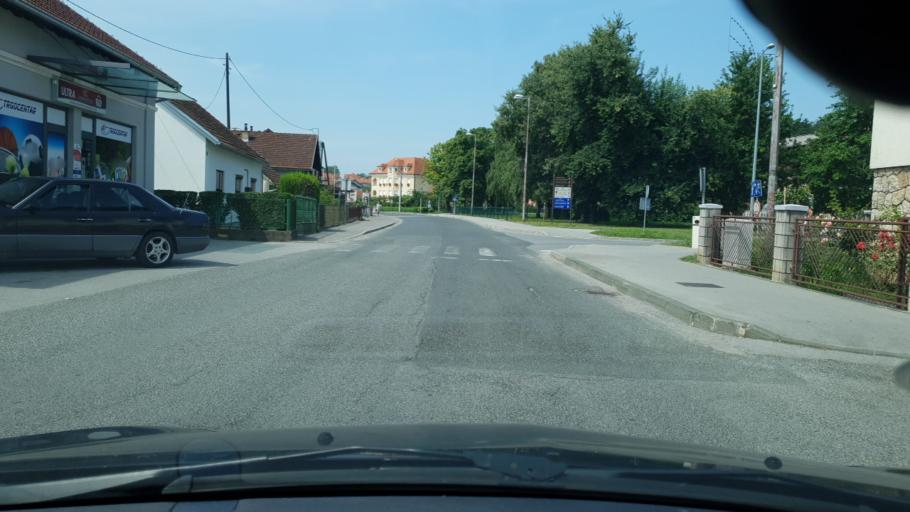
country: HR
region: Krapinsko-Zagorska
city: Bedekovcina
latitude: 46.0423
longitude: 15.9958
